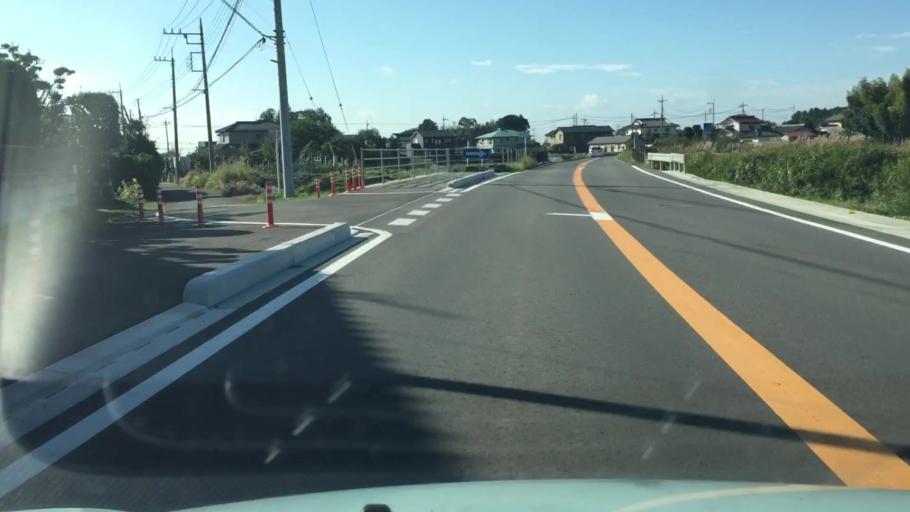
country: JP
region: Tochigi
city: Ujiie
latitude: 36.6511
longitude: 140.0210
